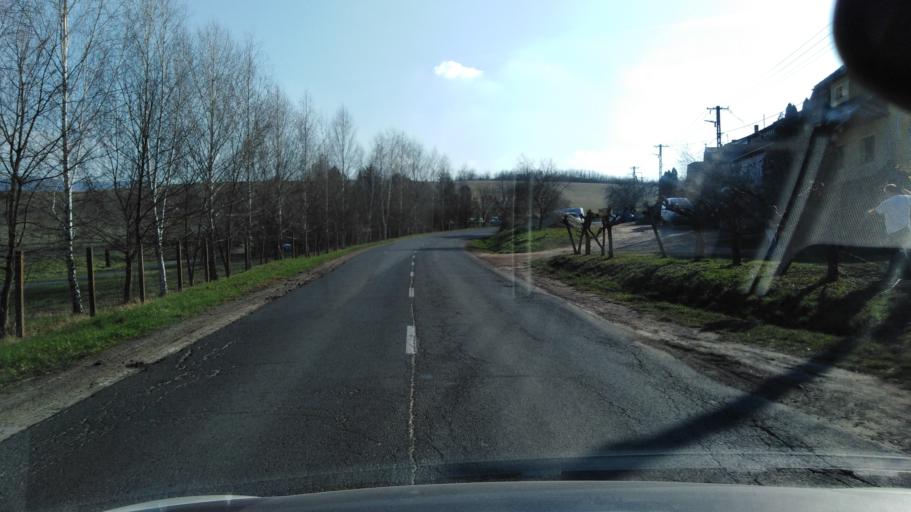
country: HU
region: Nograd
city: Batonyterenye
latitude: 47.9954
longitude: 19.8469
